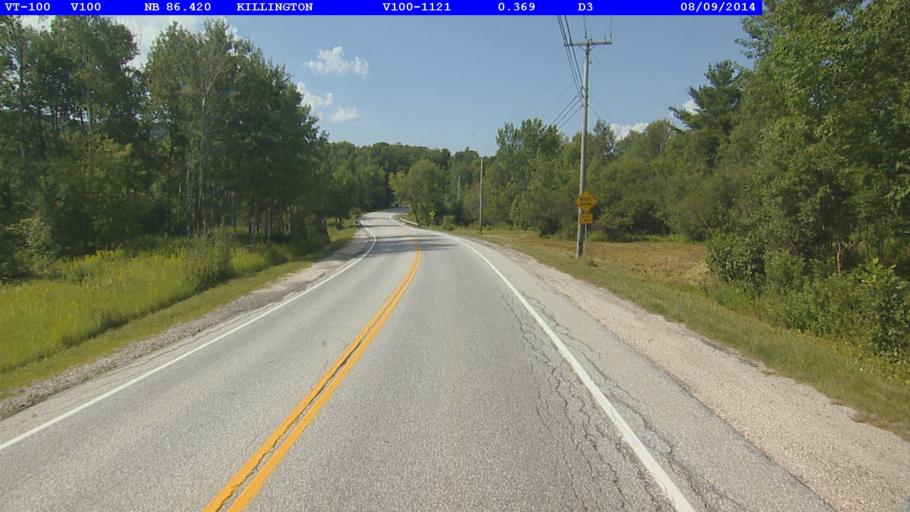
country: US
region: Vermont
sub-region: Rutland County
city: Rutland
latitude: 43.6725
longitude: -72.8077
